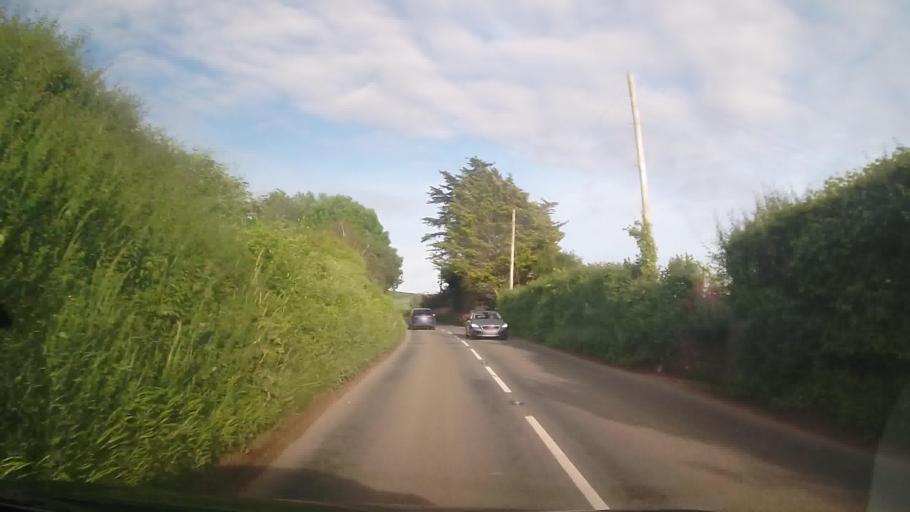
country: GB
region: England
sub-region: Devon
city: Kingsbridge
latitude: 50.2698
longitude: -3.7578
